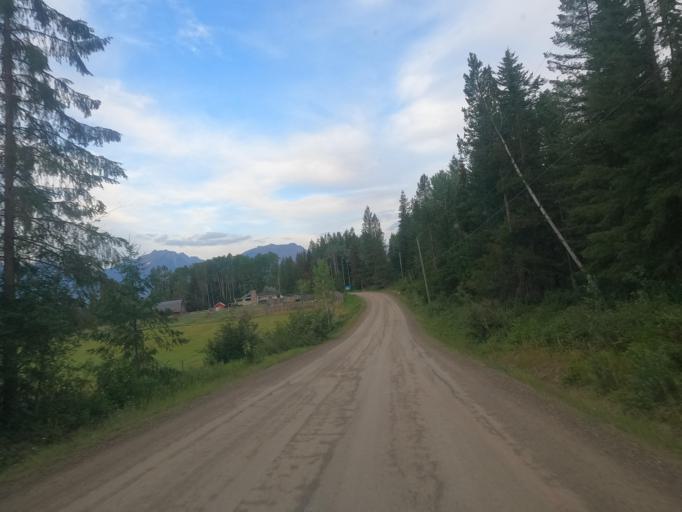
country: CA
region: British Columbia
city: Golden
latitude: 51.4457
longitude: -117.0214
